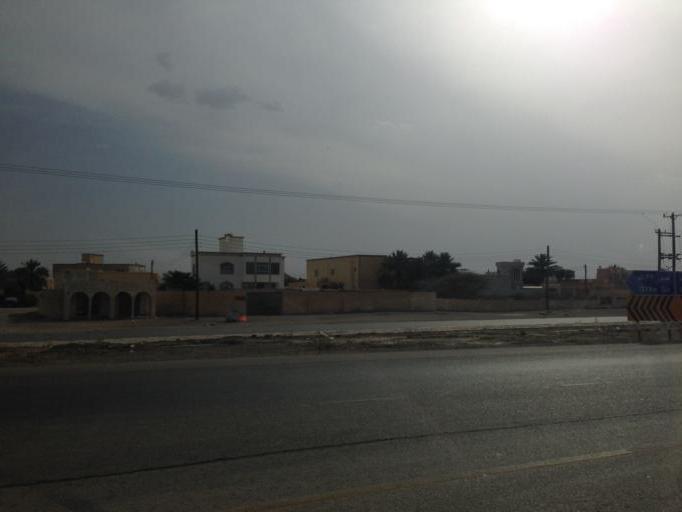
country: OM
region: Ash Sharqiyah
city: Al Qabil
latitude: 22.5877
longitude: 58.6831
